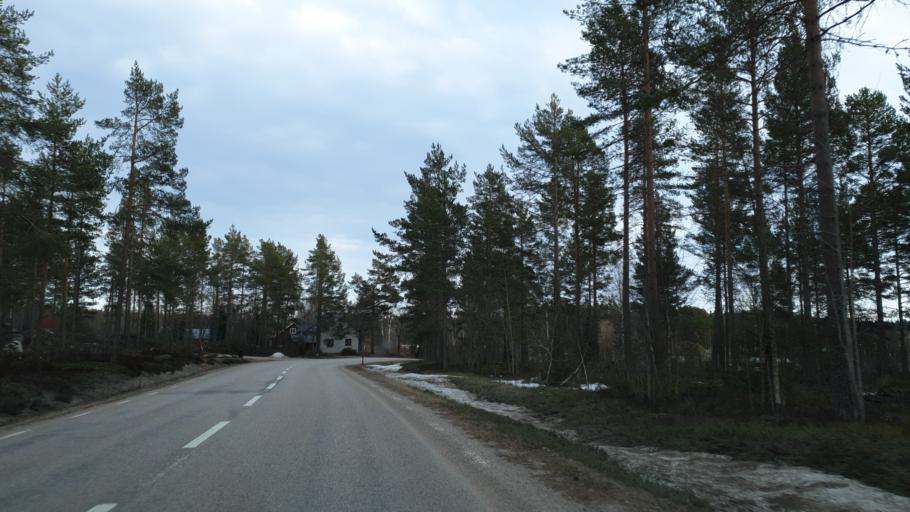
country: SE
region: Gaevleborg
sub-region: Nordanstigs Kommun
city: Bergsjoe
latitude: 61.9709
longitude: 17.2995
